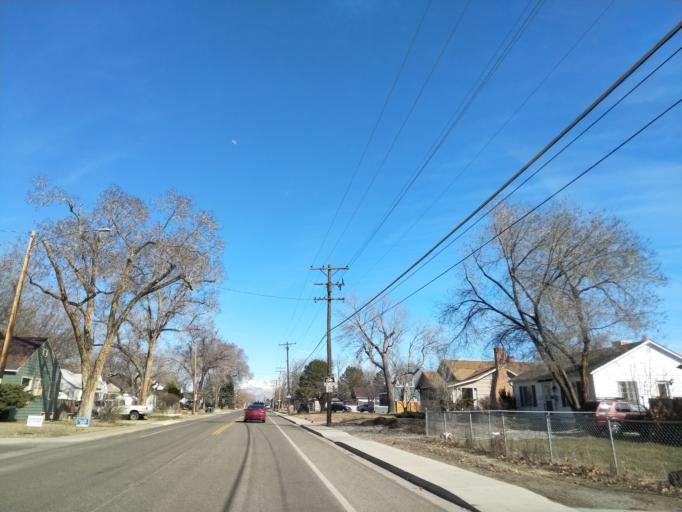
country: US
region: Colorado
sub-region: Mesa County
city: Grand Junction
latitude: 39.0846
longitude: -108.5596
